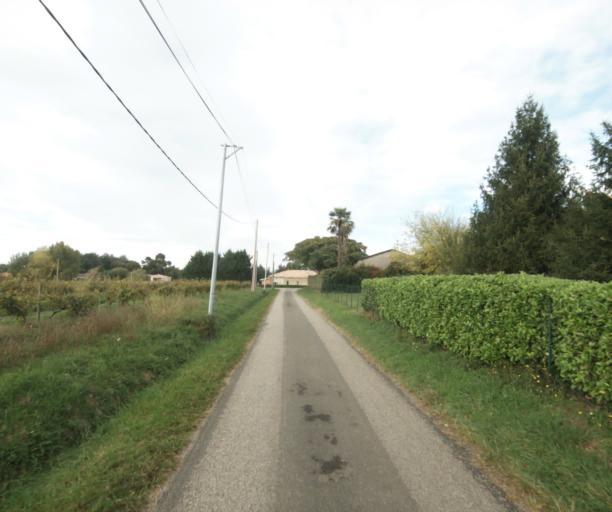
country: FR
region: Midi-Pyrenees
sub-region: Departement du Gers
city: Le Houga
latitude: 43.8549
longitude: -0.1414
